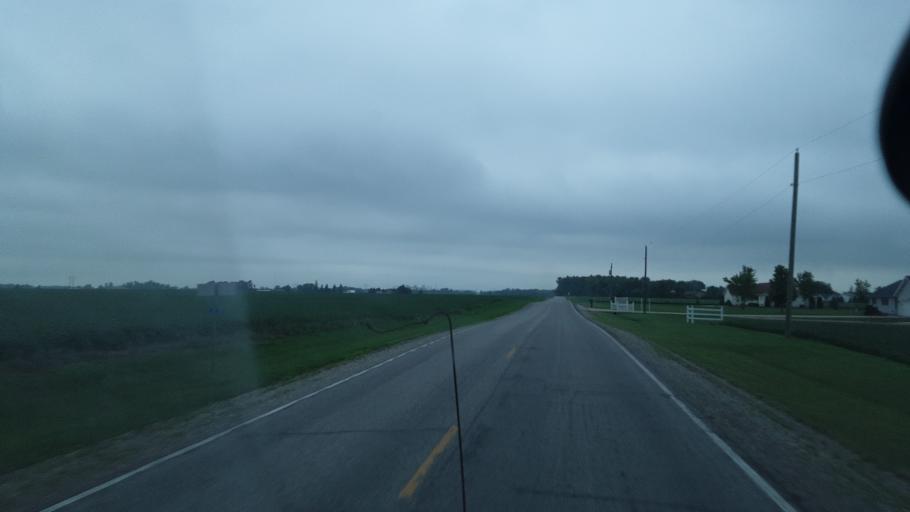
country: US
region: Indiana
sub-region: Adams County
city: Berne
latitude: 40.6428
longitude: -85.0415
